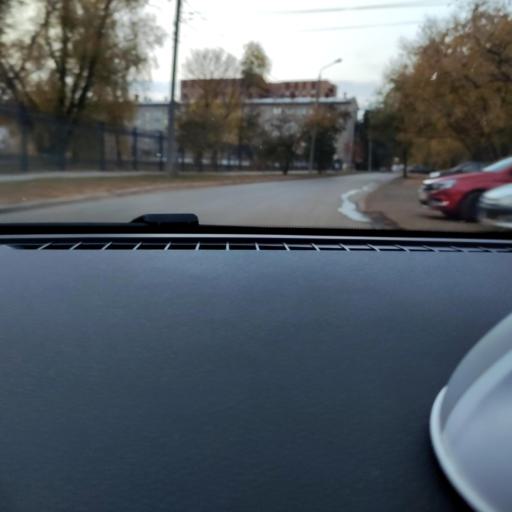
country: RU
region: Samara
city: Samara
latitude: 53.2024
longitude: 50.1662
